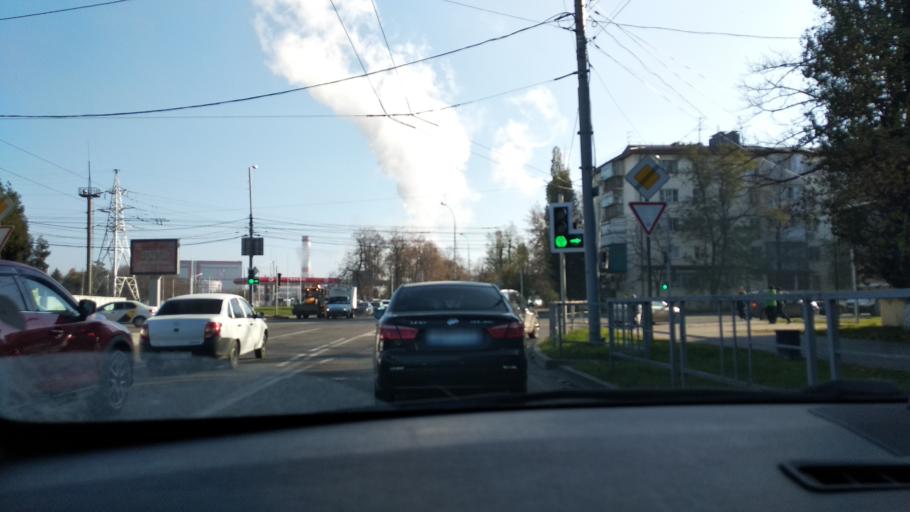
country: RU
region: Krasnodarskiy
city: Pashkovskiy
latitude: 45.0213
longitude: 39.0495
